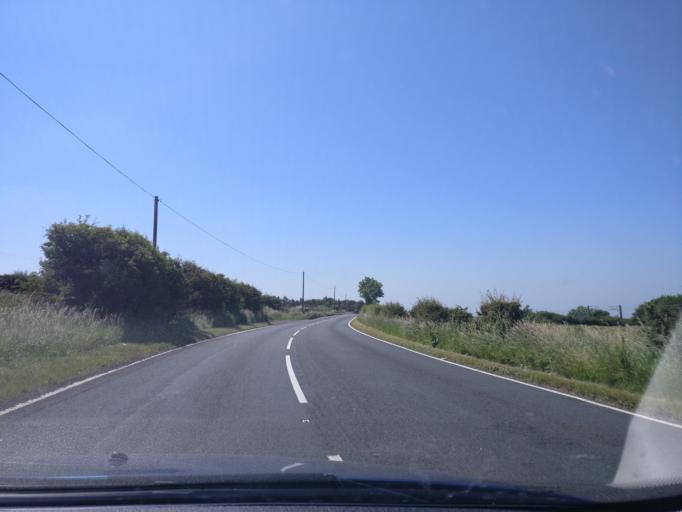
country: GB
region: Scotland
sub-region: East Lothian
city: Gullane
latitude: 55.9873
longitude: -2.8418
